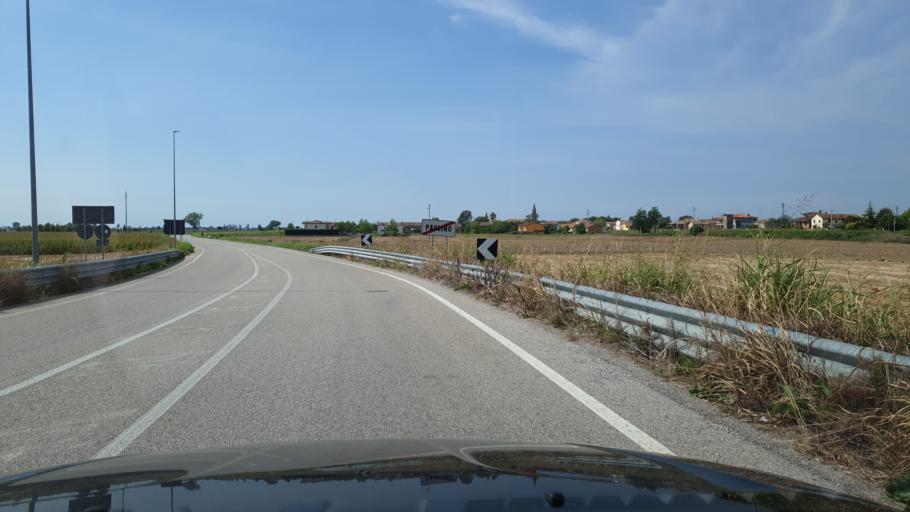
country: IT
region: Veneto
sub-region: Provincia di Rovigo
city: Pincara
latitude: 44.9987
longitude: 11.6160
